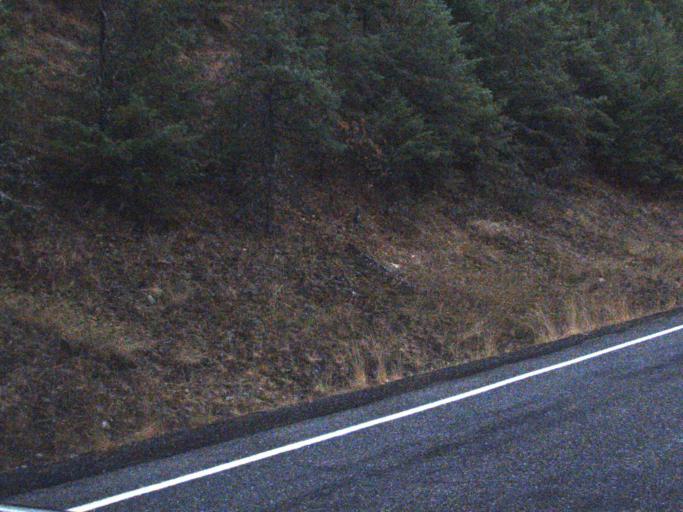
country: US
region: Washington
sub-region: Spokane County
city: Fairchild Air Force Base
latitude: 47.8373
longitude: -117.8579
